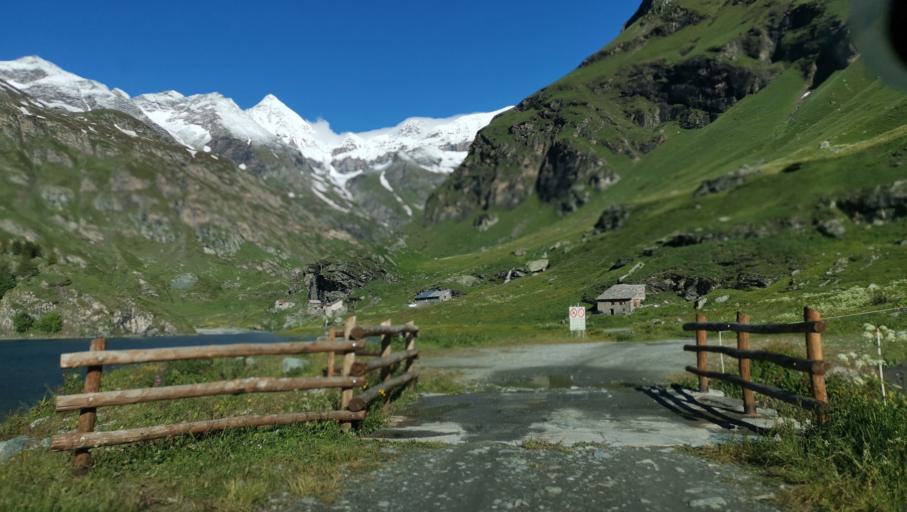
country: IT
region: Piedmont
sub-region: Provincia di Torino
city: Chianocco
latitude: 45.2082
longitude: 7.1436
